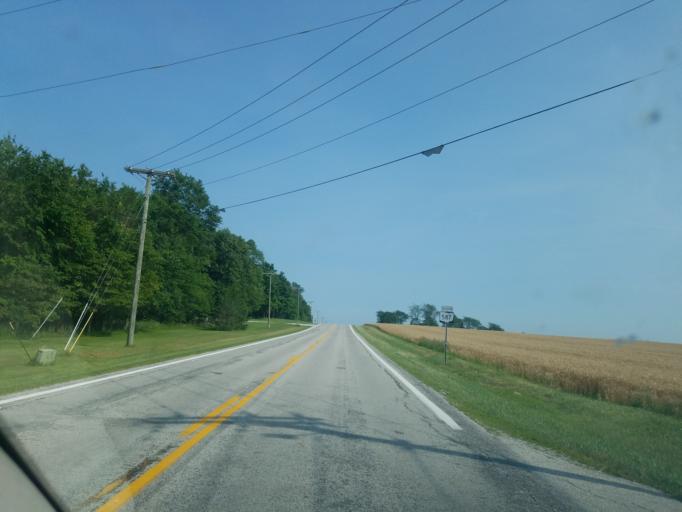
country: US
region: Ohio
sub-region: Wyandot County
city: Carey
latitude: 41.0143
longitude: -83.2853
